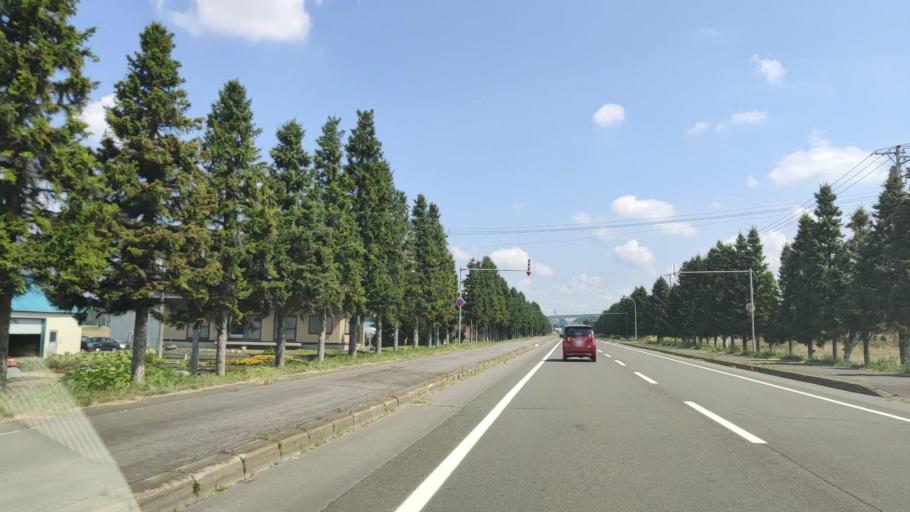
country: JP
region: Hokkaido
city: Shimo-furano
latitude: 43.4805
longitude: 142.4604
